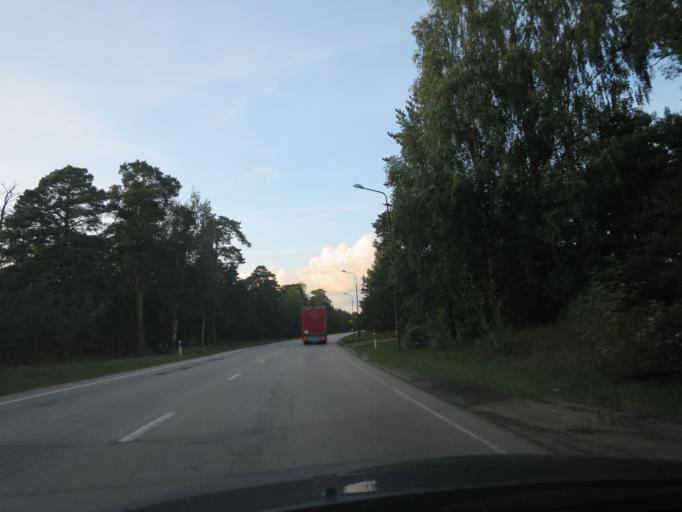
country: LV
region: Salacgrivas
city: Salacgriva
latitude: 57.7631
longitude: 24.3566
